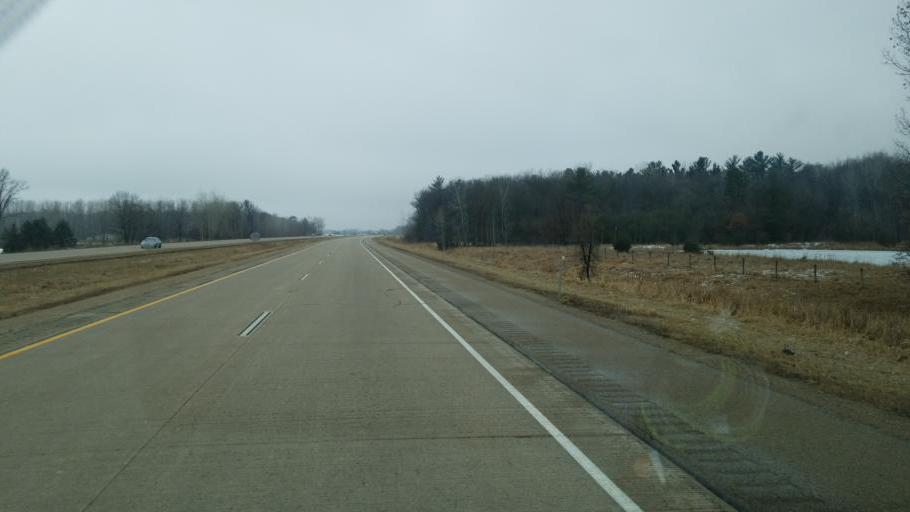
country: US
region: Wisconsin
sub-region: Waupaca County
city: Weyauwega
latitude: 44.2513
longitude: -88.8273
